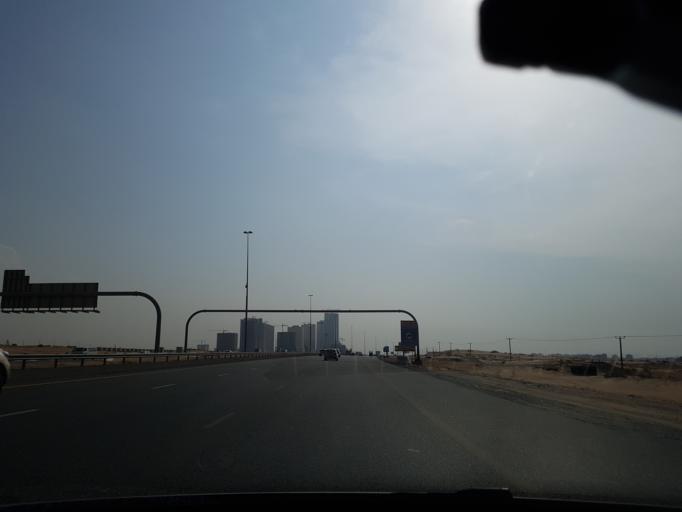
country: AE
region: Ajman
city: Ajman
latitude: 25.4088
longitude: 55.5843
